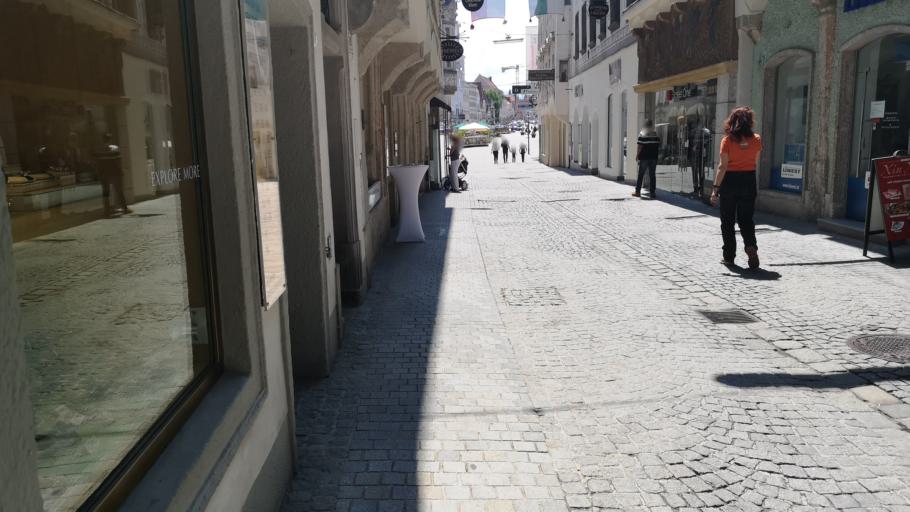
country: AT
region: Upper Austria
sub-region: Steyr Stadt
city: Steyr
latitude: 48.0408
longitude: 14.4203
